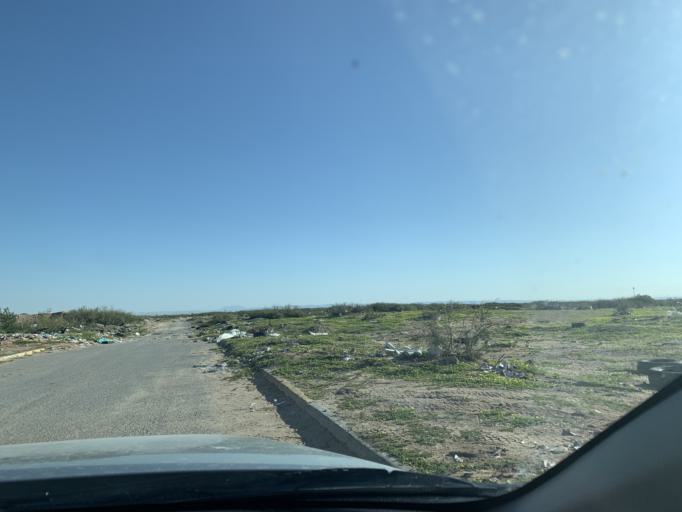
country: US
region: Texas
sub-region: El Paso County
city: San Elizario
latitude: 31.5775
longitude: -106.3435
